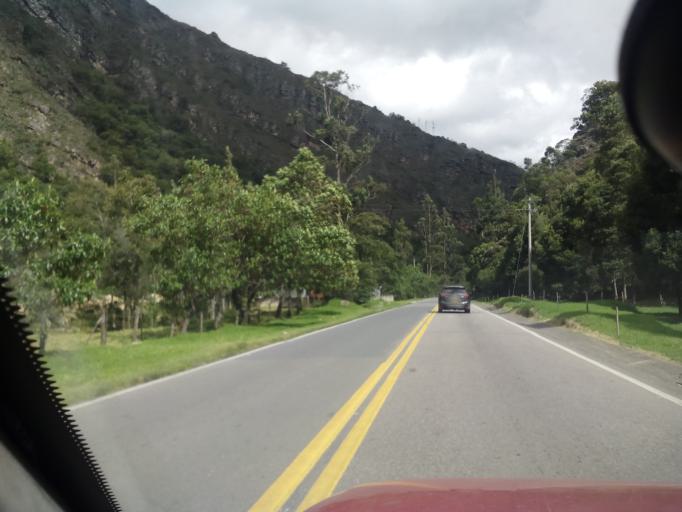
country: CO
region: Boyaca
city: Arcabuco
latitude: 5.7465
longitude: -73.4297
